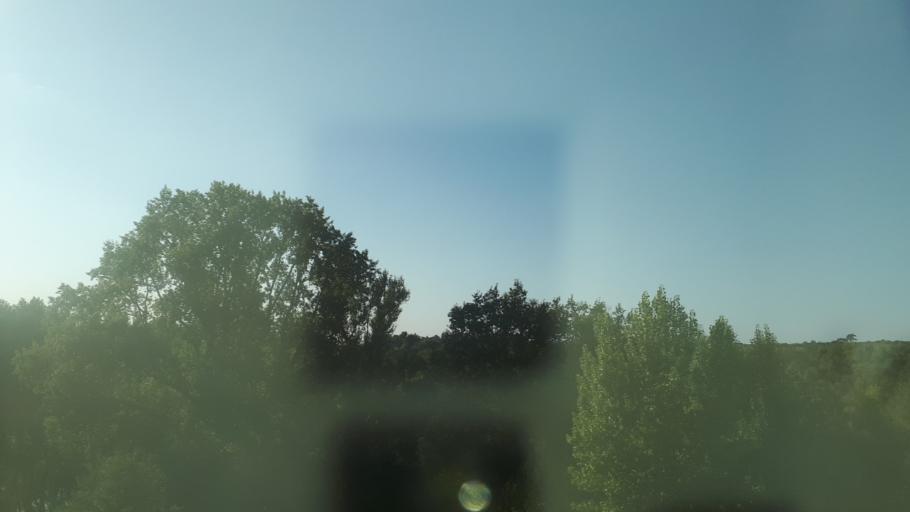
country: FR
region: Centre
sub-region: Departement d'Indre-et-Loire
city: Vouvray
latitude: 47.4012
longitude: 0.8059
